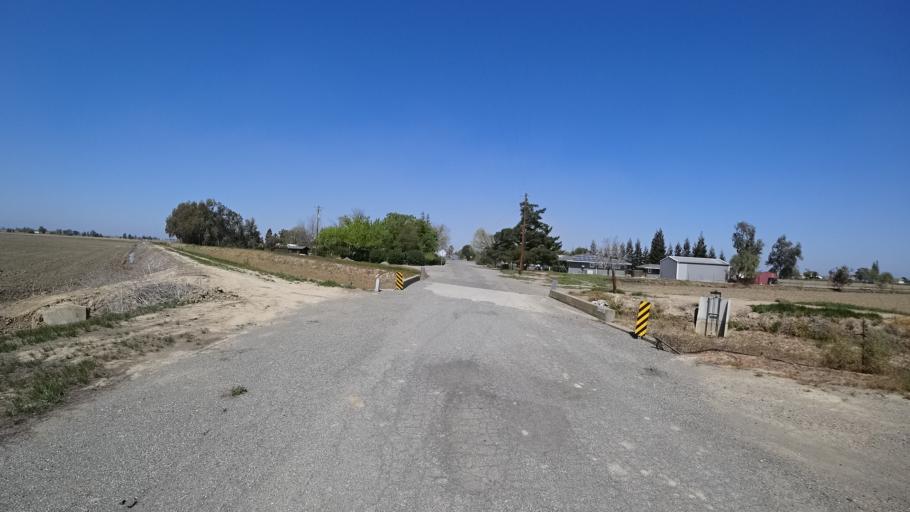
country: US
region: California
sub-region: Glenn County
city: Willows
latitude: 39.5214
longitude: -122.1169
